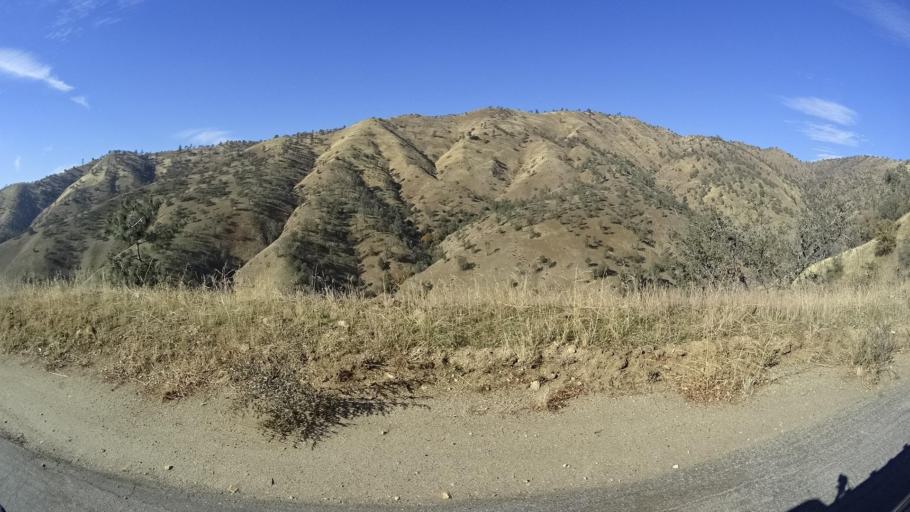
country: US
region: California
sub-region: Kern County
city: Bear Valley Springs
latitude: 35.3347
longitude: -118.5832
